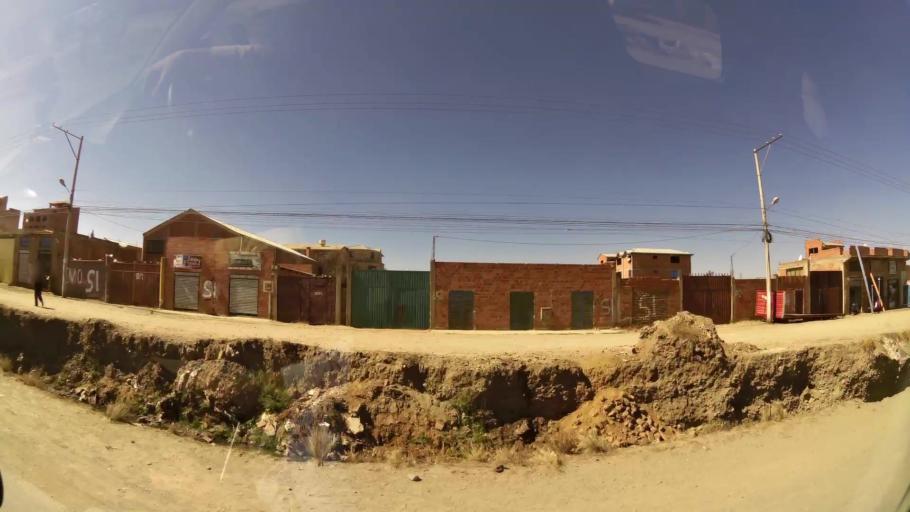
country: BO
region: La Paz
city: La Paz
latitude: -16.5558
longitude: -68.2104
